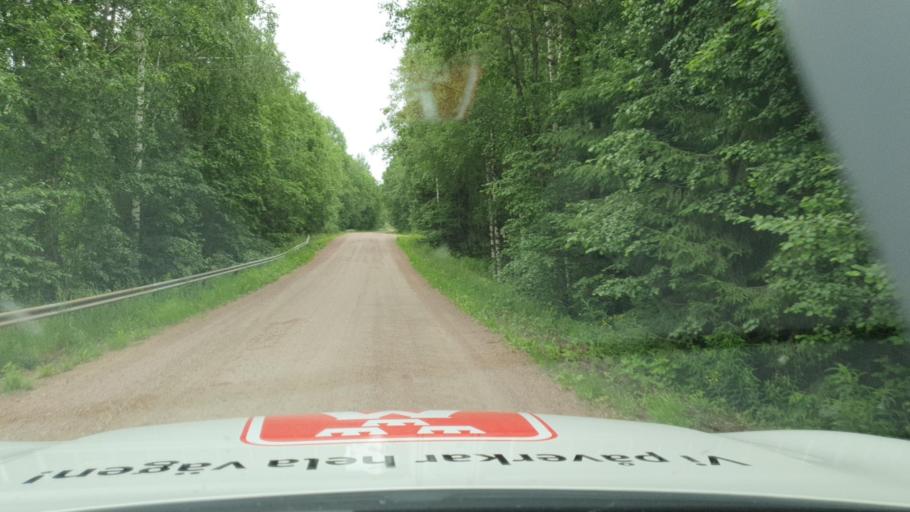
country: SE
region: Vaermland
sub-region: Filipstads Kommun
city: Filipstad
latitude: 59.5420
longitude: 13.9702
